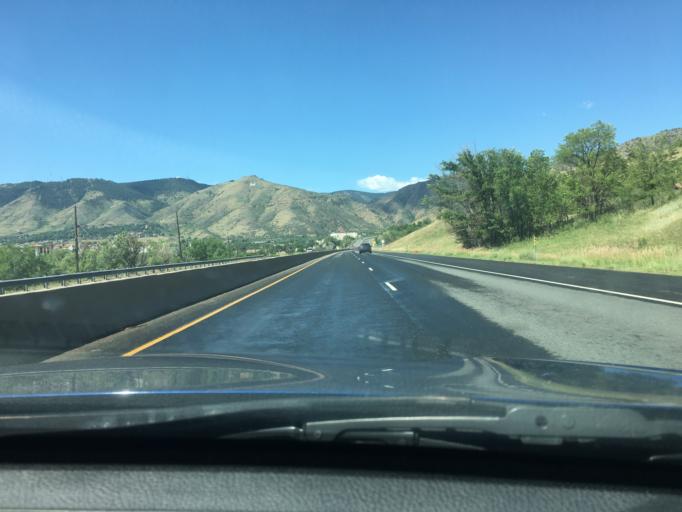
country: US
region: Colorado
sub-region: Jefferson County
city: Golden
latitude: 39.7659
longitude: -105.2114
